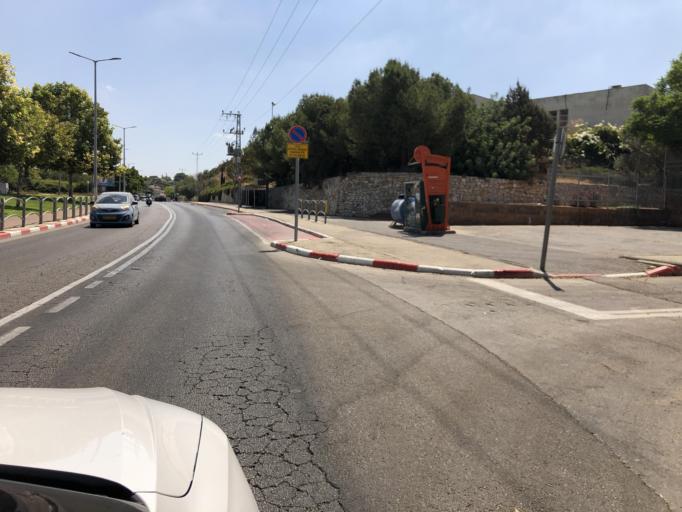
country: IL
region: Central District
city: Rosh Ha'Ayin
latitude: 32.0976
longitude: 34.9596
